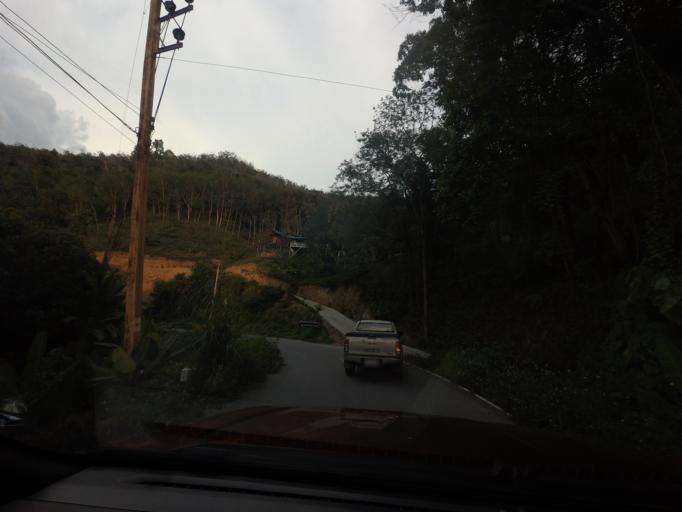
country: TH
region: Yala
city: Than To
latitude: 6.0084
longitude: 101.2276
